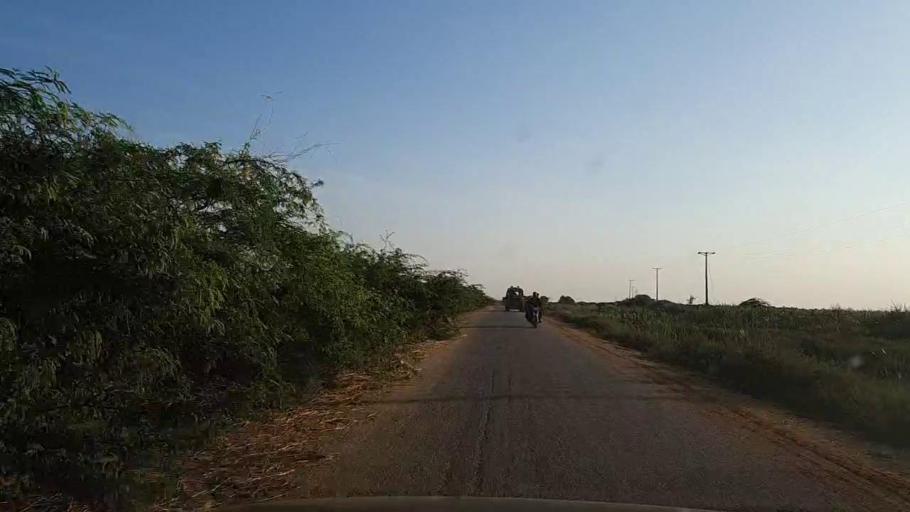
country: PK
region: Sindh
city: Thatta
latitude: 24.6386
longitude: 67.9125
